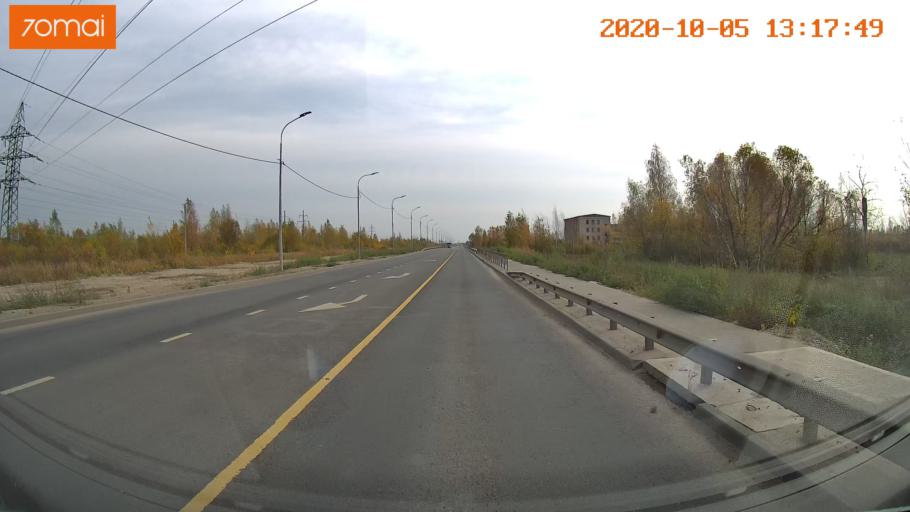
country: RU
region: Ivanovo
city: Novo-Talitsy
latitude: 56.9838
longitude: 40.9125
